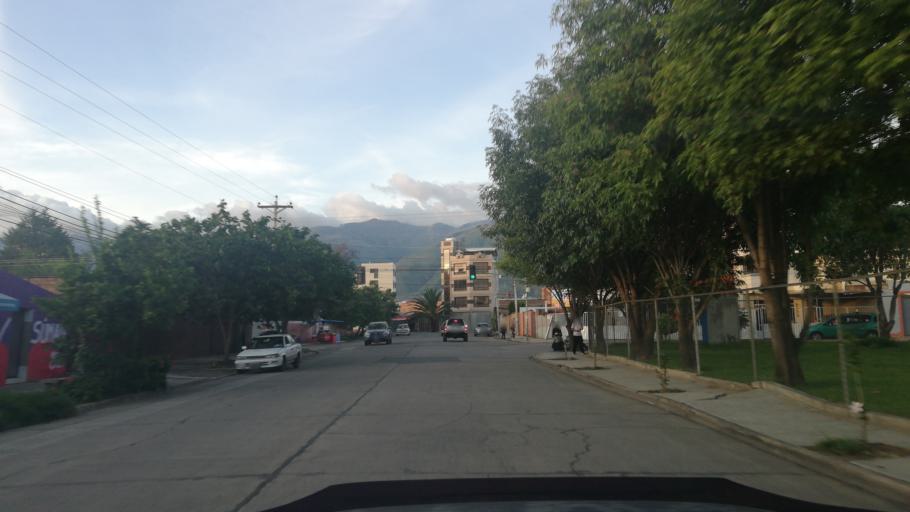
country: BO
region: Cochabamba
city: Cochabamba
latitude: -17.3745
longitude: -66.1873
